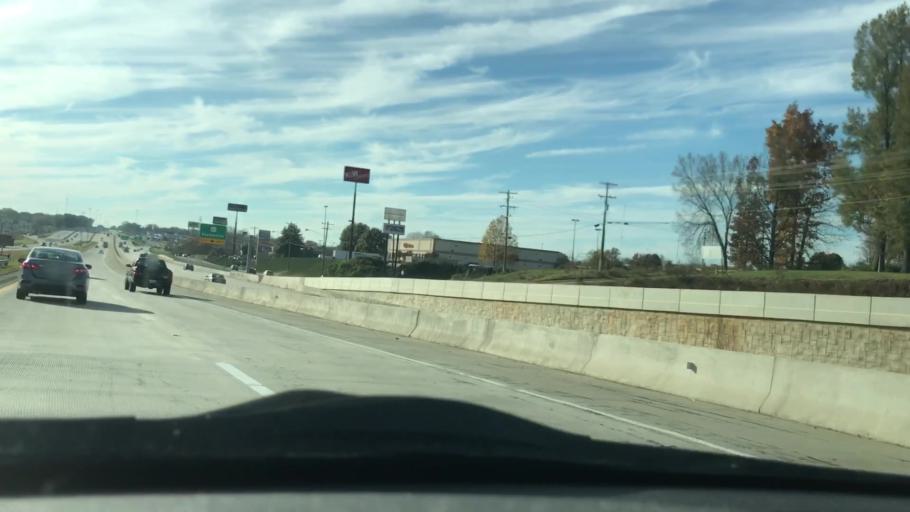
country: US
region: North Carolina
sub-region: Iredell County
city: Statesville
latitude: 35.8092
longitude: -80.8654
